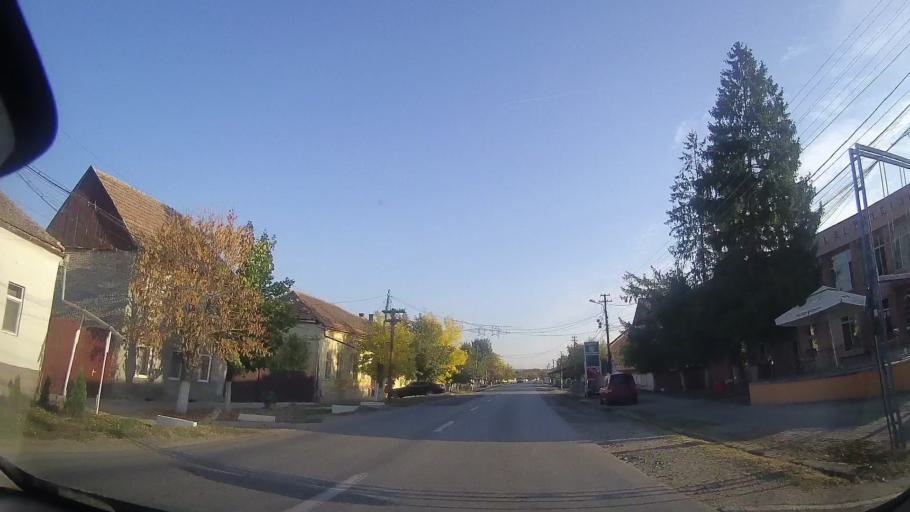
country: RO
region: Timis
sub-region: Comuna Pischia
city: Pischia
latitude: 45.9043
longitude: 21.3402
